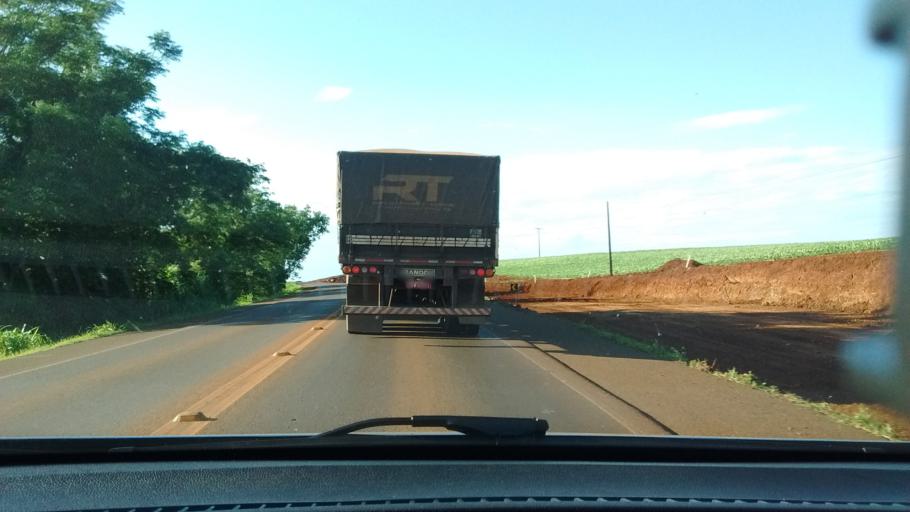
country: BR
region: Parana
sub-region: Cascavel
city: Cascavel
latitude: -25.2184
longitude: -53.5954
